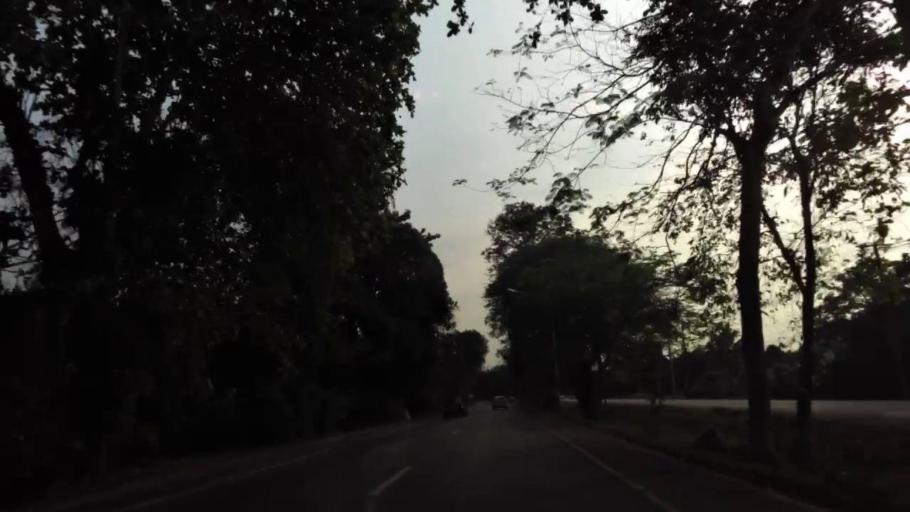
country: TH
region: Chanthaburi
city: Chanthaburi
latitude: 12.5656
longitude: 102.1614
